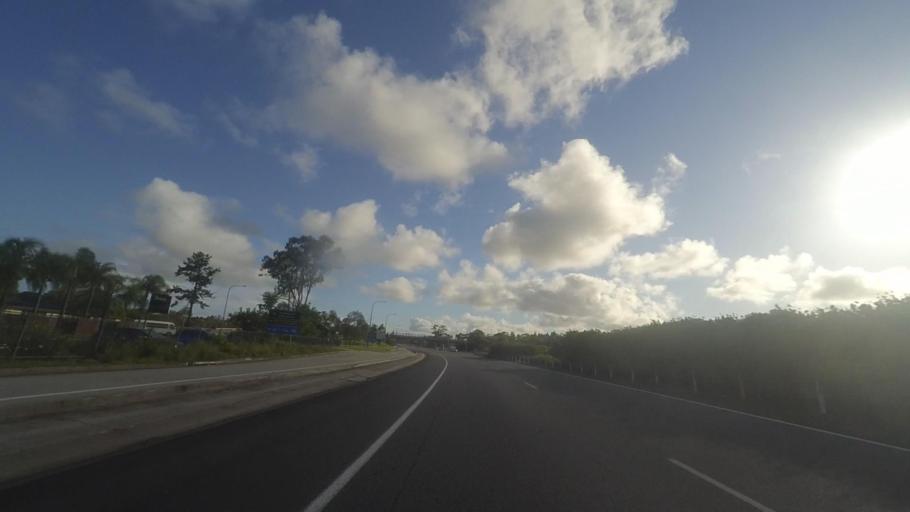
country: AU
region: New South Wales
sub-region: Great Lakes
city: Nabiac
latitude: -32.0986
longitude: 152.3763
